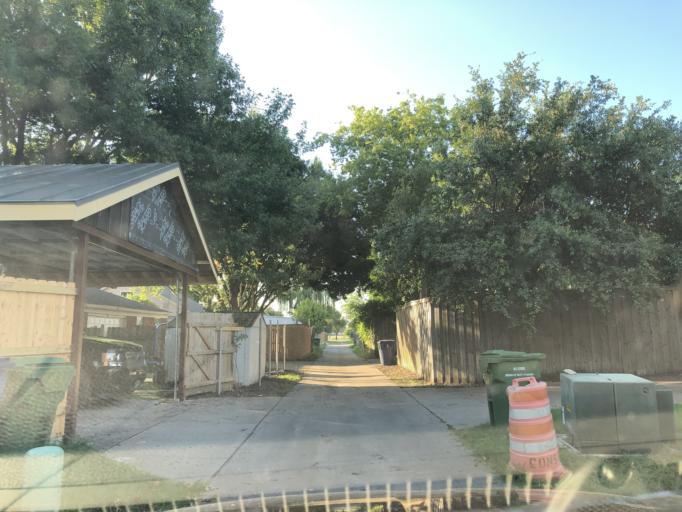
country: US
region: Texas
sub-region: Dallas County
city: Garland
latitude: 32.8461
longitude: -96.6215
